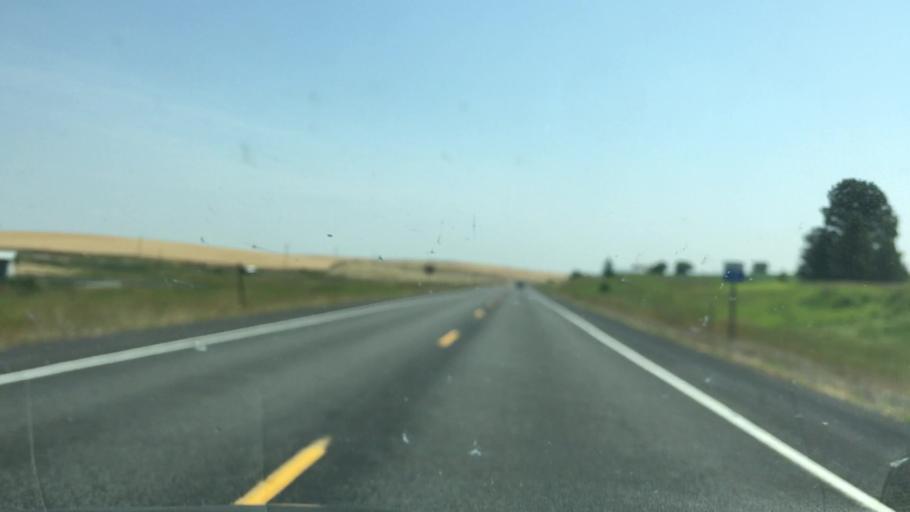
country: US
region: Idaho
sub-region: Lewis County
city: Nezperce
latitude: 46.2304
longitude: -116.4588
